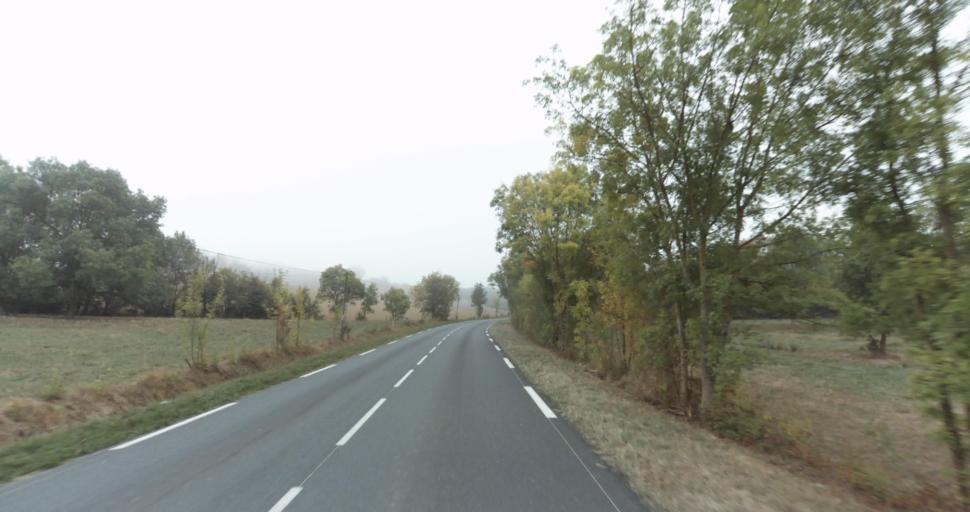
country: FR
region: Midi-Pyrenees
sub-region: Departement du Gers
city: Preignan
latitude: 43.6796
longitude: 0.6190
